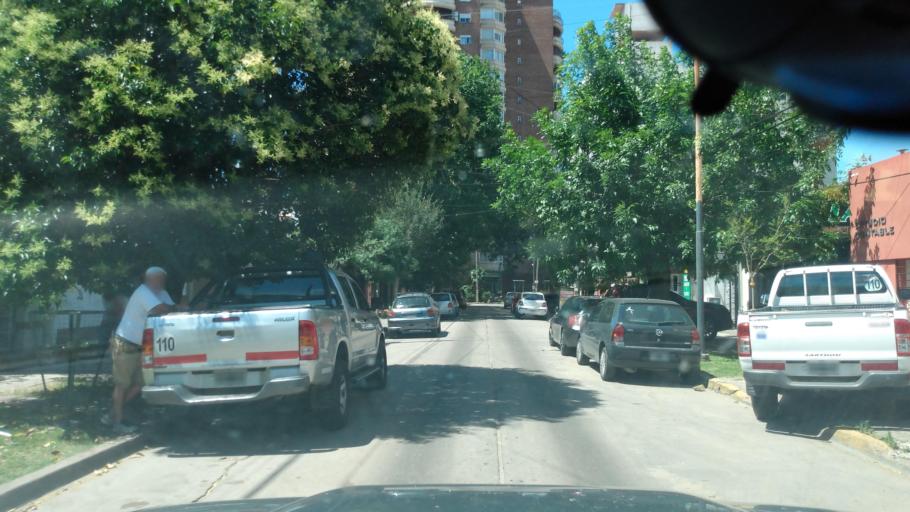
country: AR
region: Buenos Aires
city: Hurlingham
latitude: -34.5420
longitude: -58.7059
